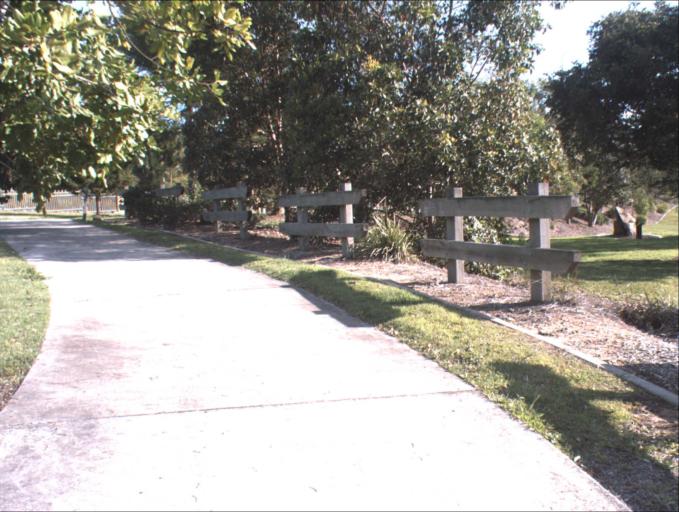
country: AU
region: Queensland
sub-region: Logan
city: Chambers Flat
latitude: -27.7708
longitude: 153.1020
